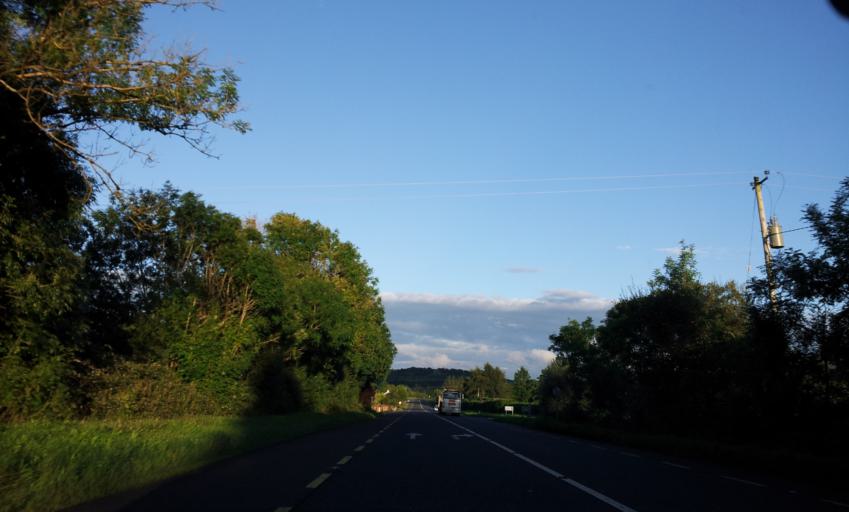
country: IE
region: Munster
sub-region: County Limerick
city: Abbeyfeale
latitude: 52.3873
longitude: -9.2385
